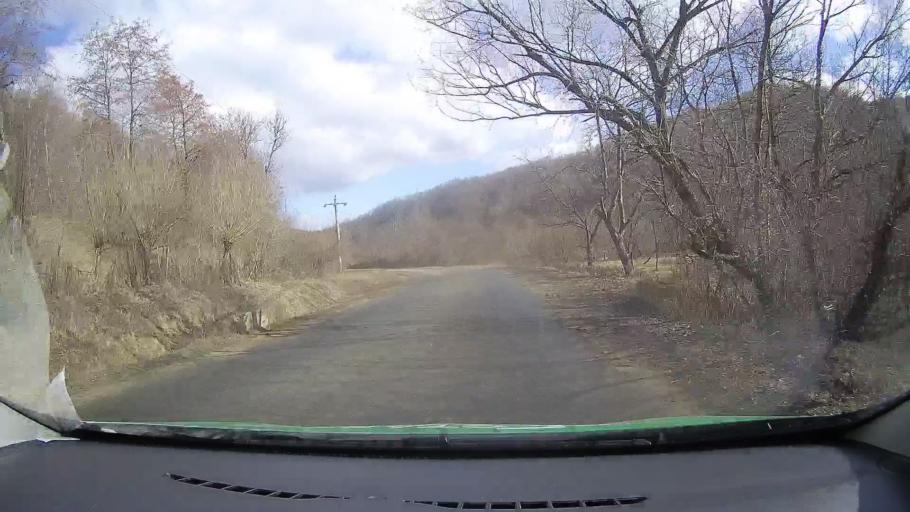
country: RO
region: Dambovita
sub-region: Comuna Motaeni
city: Motaeni
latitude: 45.1051
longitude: 25.4415
